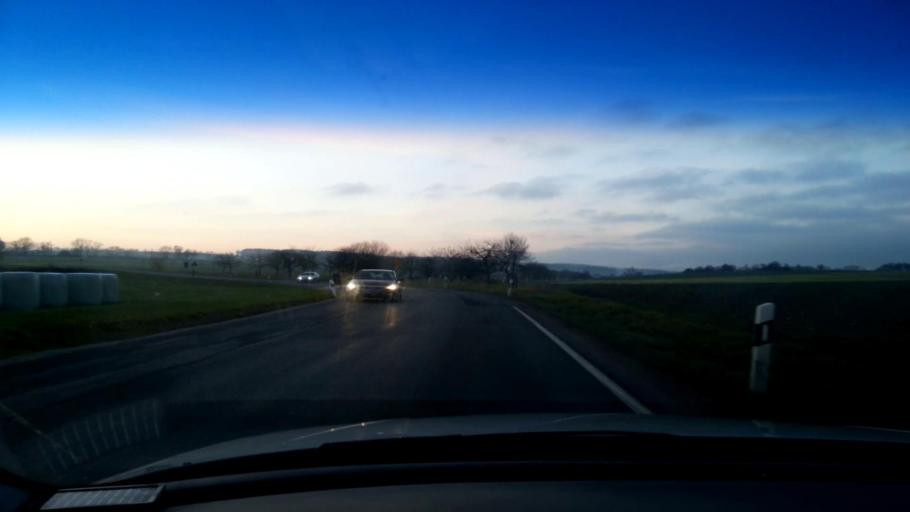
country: DE
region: Bavaria
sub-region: Upper Franconia
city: Pommersfelden
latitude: 49.7803
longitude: 10.8327
